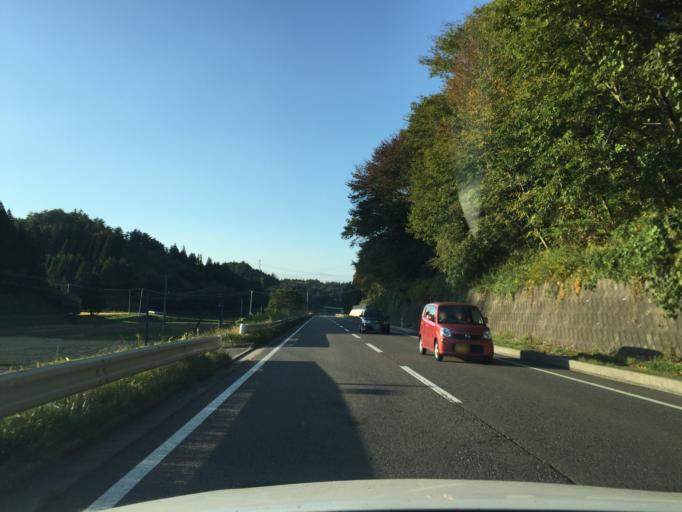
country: JP
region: Fukushima
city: Ishikawa
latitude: 37.1864
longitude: 140.6450
